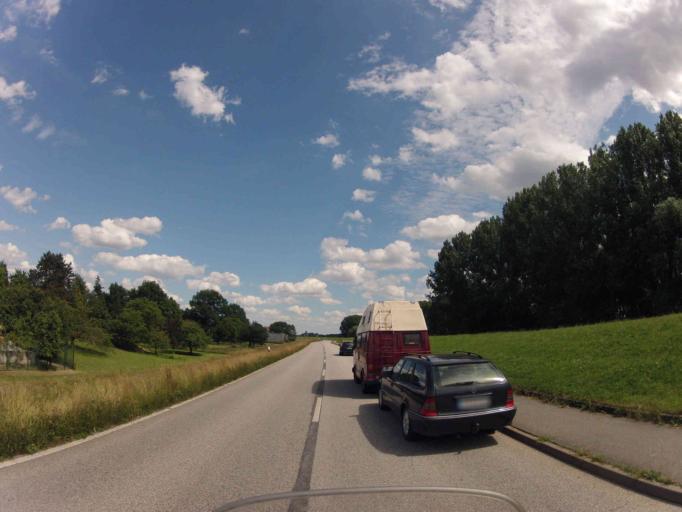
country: DE
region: Lower Saxony
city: Winsen
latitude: 53.3991
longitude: 10.1743
